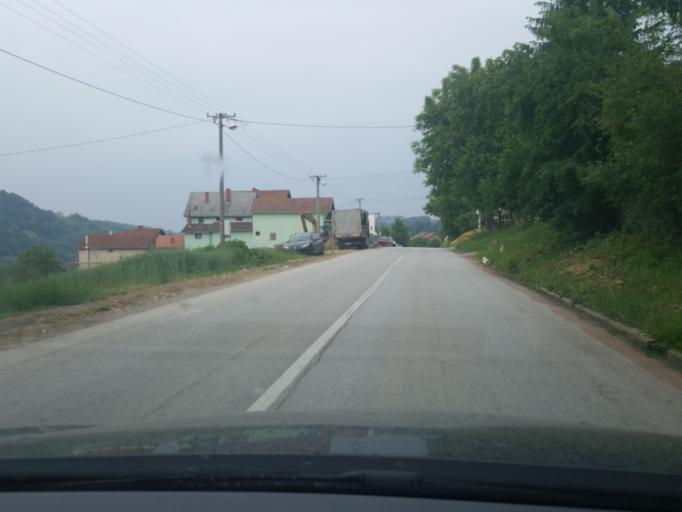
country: RS
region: Central Serbia
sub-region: Kolubarski Okrug
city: Valjevo
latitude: 44.2564
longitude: 19.8525
